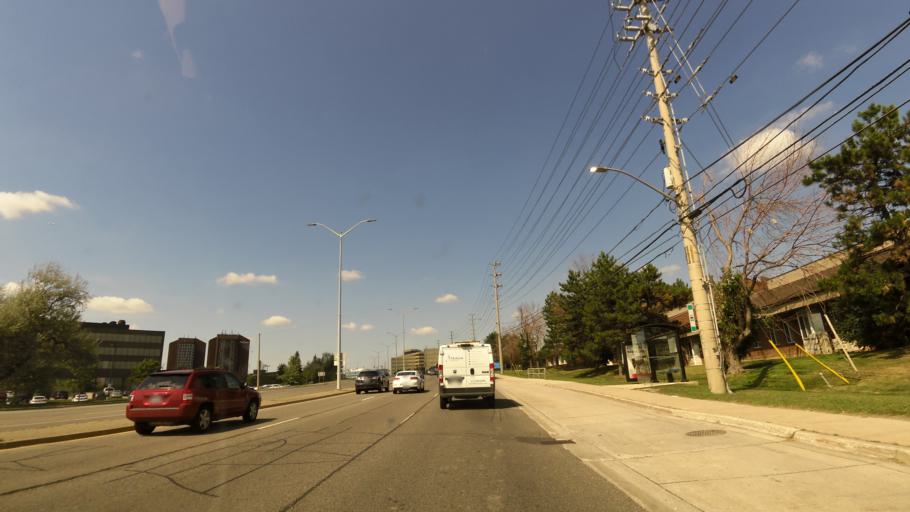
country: CA
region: Ontario
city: Mississauga
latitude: 43.5982
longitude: -79.7388
